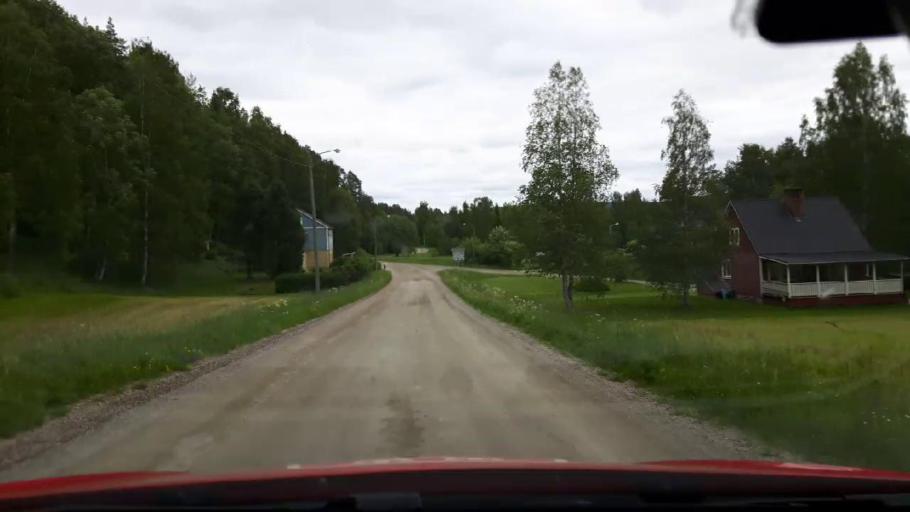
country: SE
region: Jaemtland
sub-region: Ragunda Kommun
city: Hammarstrand
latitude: 63.1604
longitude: 16.2232
